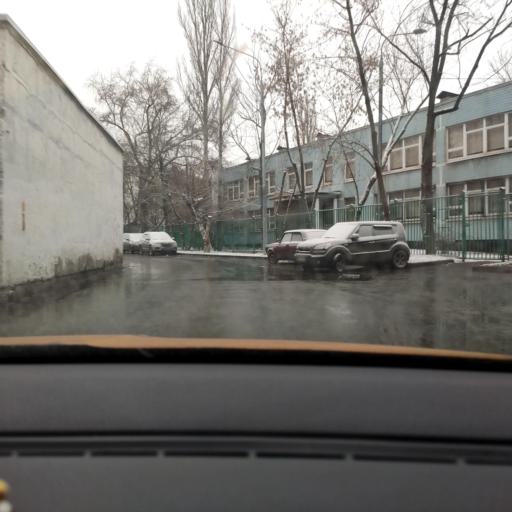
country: RU
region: Moskovskaya
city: Kur'yanovo
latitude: 55.6576
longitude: 37.7034
